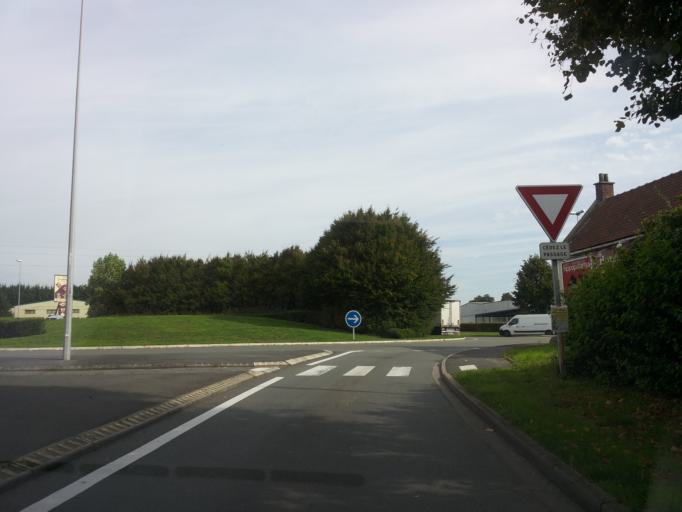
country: FR
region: Nord-Pas-de-Calais
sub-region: Departement du Nord
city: Raillencourt-Sainte-Olle
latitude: 50.1848
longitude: 3.1889
